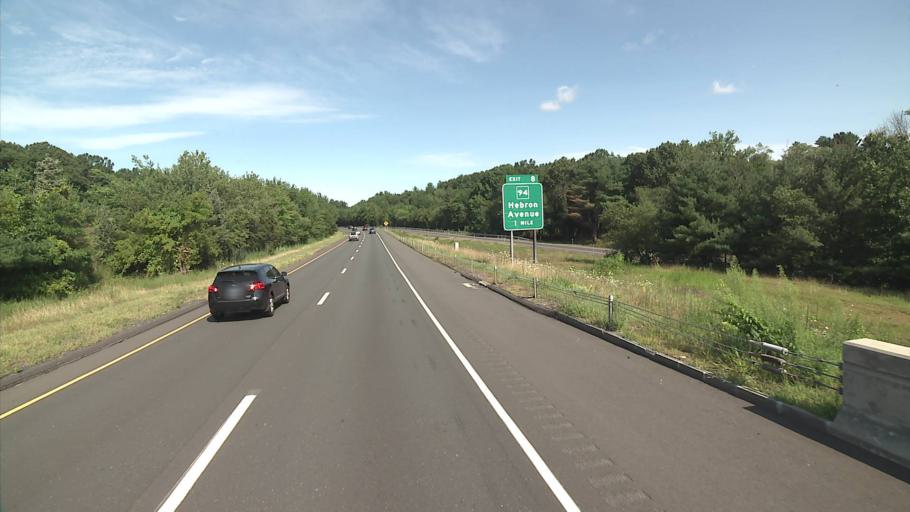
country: US
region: Connecticut
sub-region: Hartford County
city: Glastonbury Center
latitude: 41.7034
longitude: -72.5700
